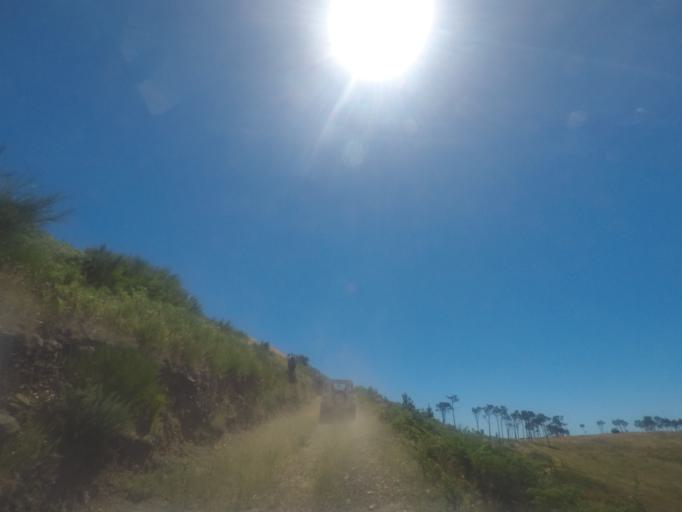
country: PT
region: Madeira
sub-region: Funchal
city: Nossa Senhora do Monte
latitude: 32.7164
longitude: -16.9134
